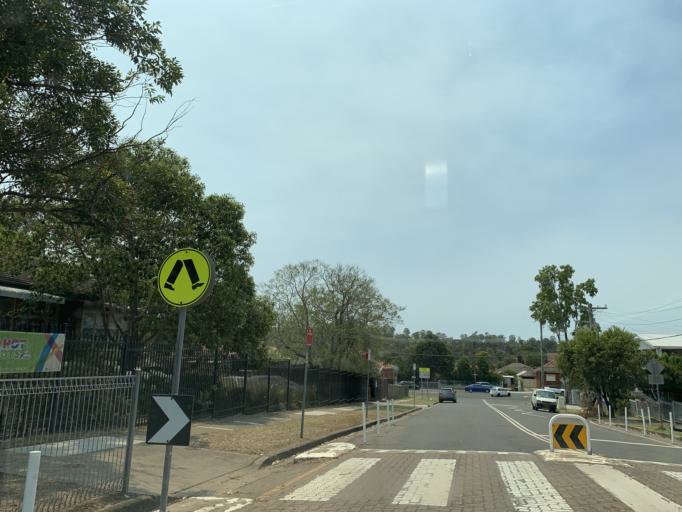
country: AU
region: New South Wales
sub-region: Blacktown
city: Blacktown
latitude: -33.7774
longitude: 150.9258
